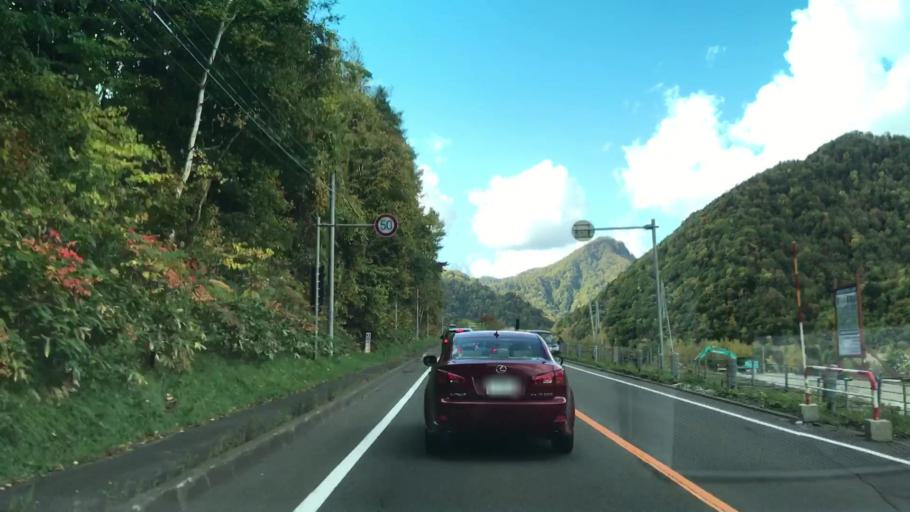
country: JP
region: Hokkaido
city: Sapporo
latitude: 42.9690
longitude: 141.1801
